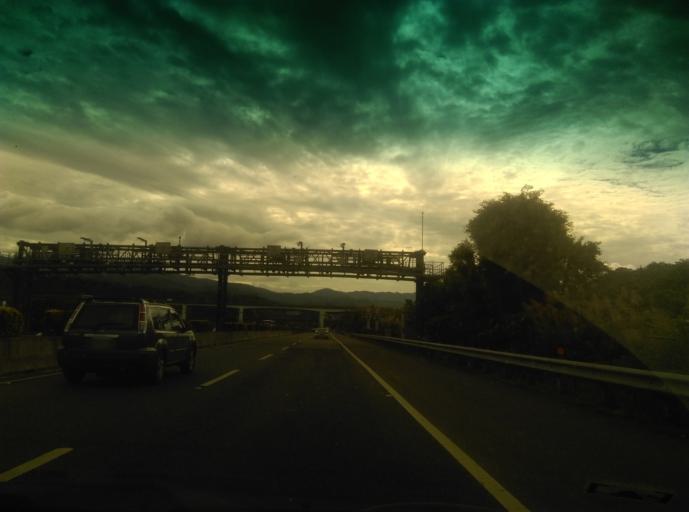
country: TW
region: Taiwan
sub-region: Keelung
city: Keelung
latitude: 25.1101
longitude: 121.7261
